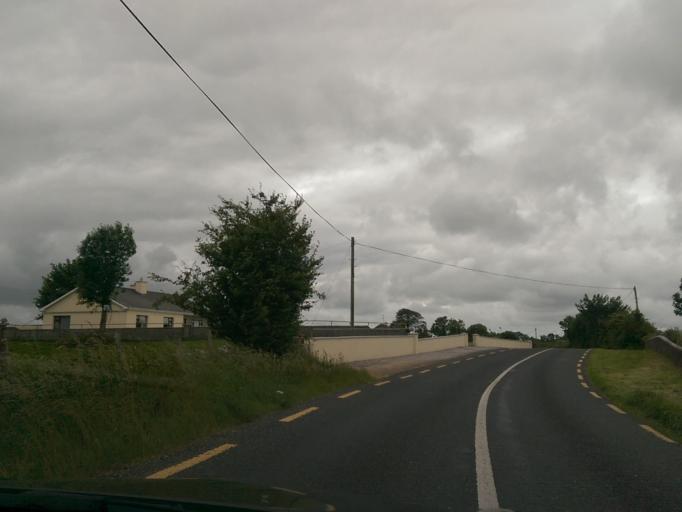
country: IE
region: Connaught
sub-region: County Galway
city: Loughrea
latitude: 53.2724
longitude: -8.5335
